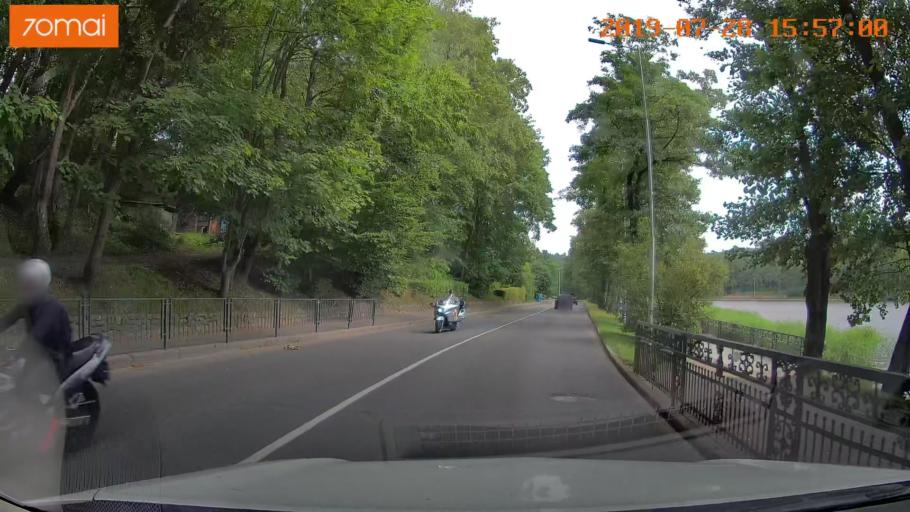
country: RU
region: Kaliningrad
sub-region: Gorod Svetlogorsk
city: Svetlogorsk
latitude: 54.9392
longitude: 20.1512
